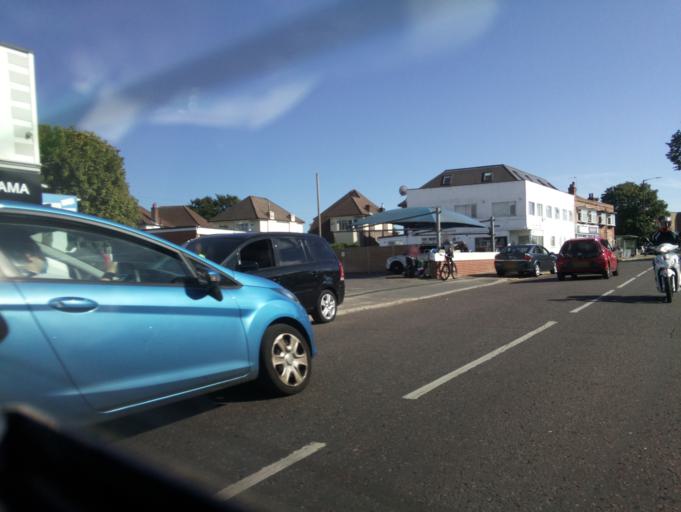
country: GB
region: England
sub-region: Bournemouth
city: Bournemouth
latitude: 50.7575
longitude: -1.8727
